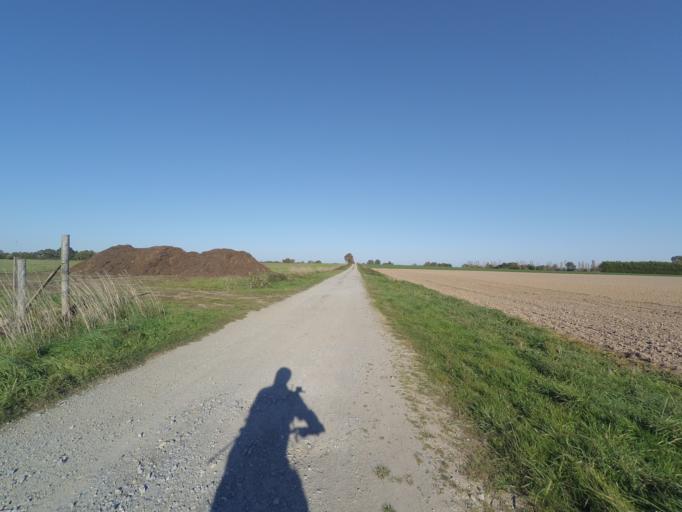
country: FR
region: Pays de la Loire
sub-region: Departement de la Loire-Atlantique
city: La Planche
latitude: 47.0223
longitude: -1.3968
